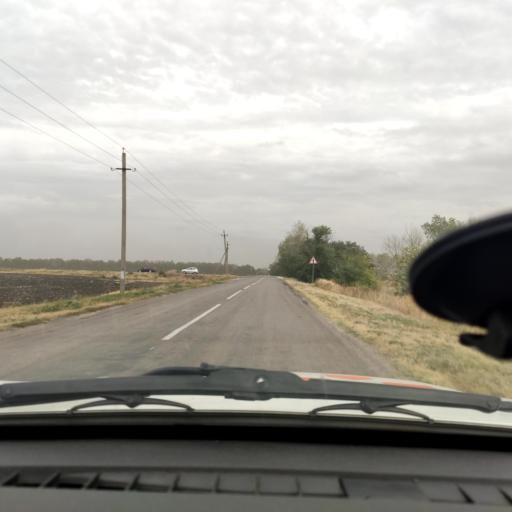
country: RU
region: Voronezj
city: Ramon'
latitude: 52.0064
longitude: 39.1608
